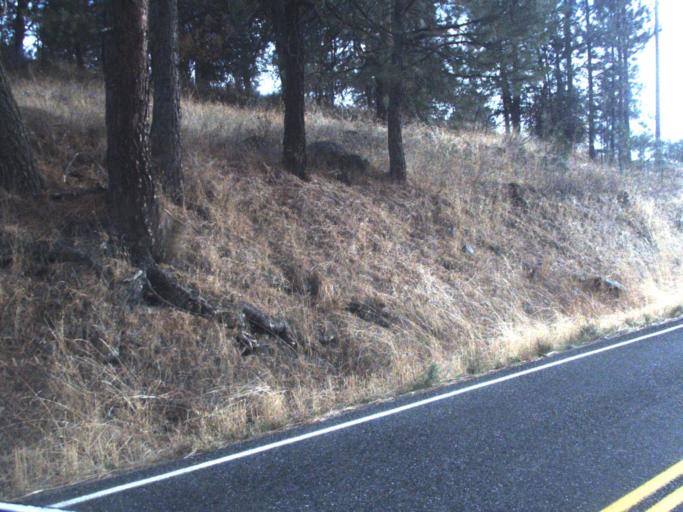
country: US
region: Washington
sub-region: Stevens County
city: Kettle Falls
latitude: 48.4212
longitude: -118.1706
